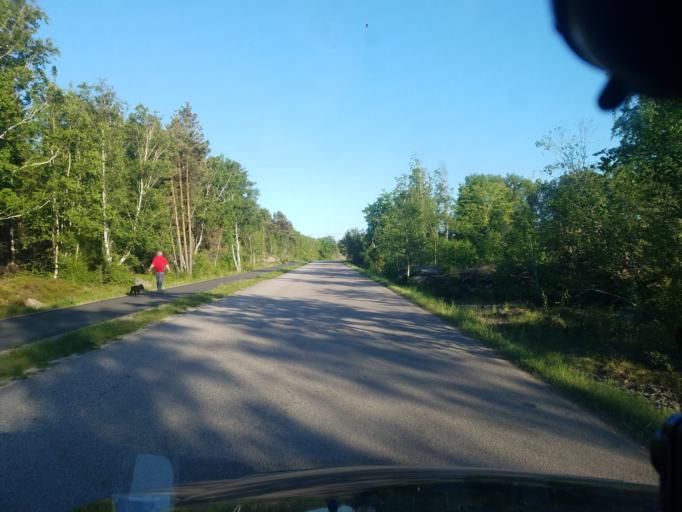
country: SE
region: Vaestra Goetaland
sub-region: Lysekils Kommun
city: Lysekil
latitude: 58.2937
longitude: 11.4527
